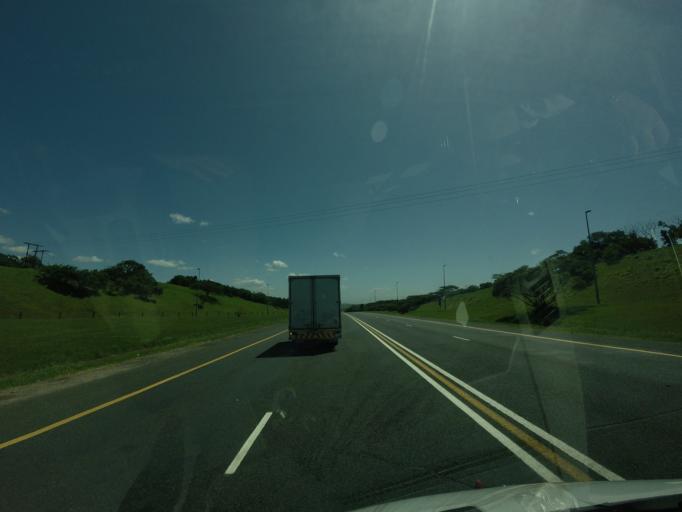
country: ZA
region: KwaZulu-Natal
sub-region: uThungulu District Municipality
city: eSikhawini
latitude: -28.9504
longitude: 31.7425
